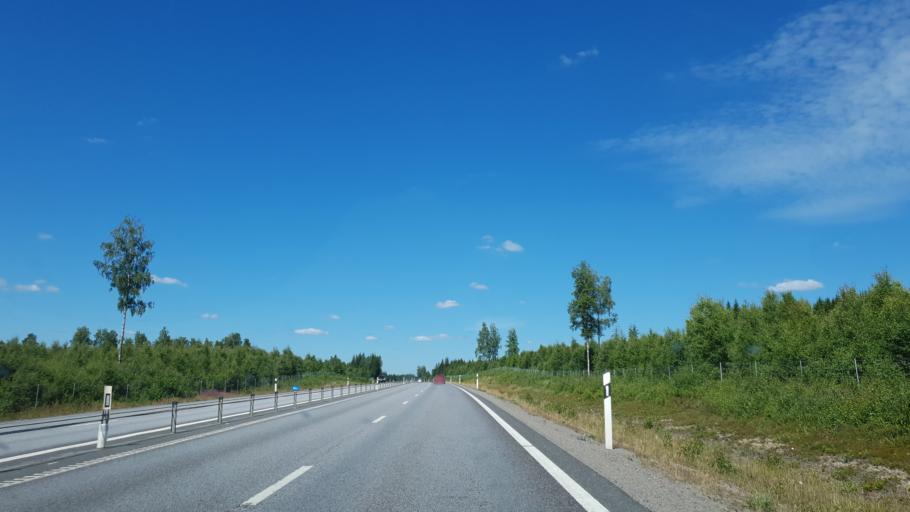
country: SE
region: Kronoberg
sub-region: Vaxjo Kommun
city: Gemla
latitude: 56.9054
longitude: 14.6590
